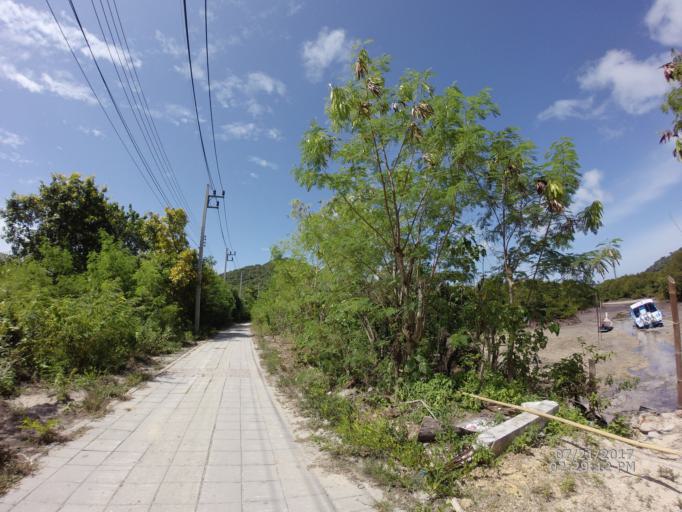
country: TH
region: Phangnga
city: Ban Phru Nai
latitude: 7.7615
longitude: 98.7665
